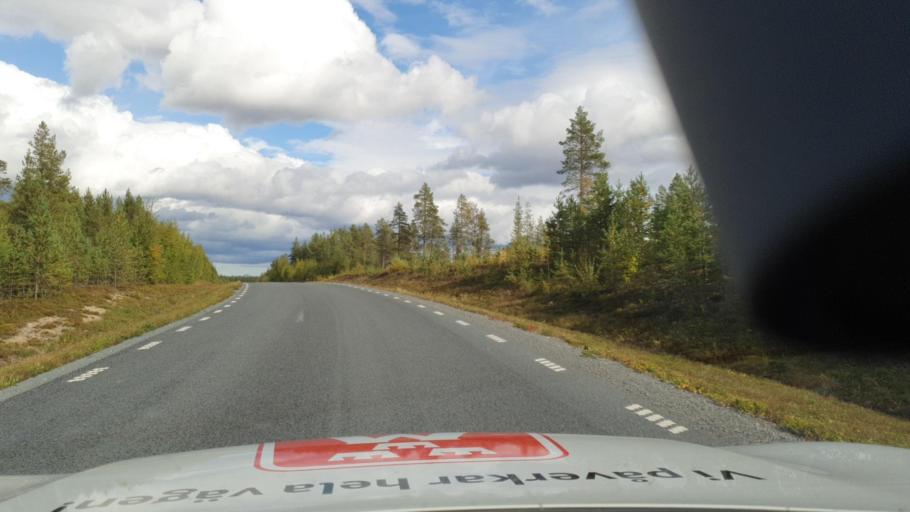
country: SE
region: Dalarna
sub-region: Alvdalens Kommun
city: AElvdalen
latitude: 61.6748
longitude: 13.3396
